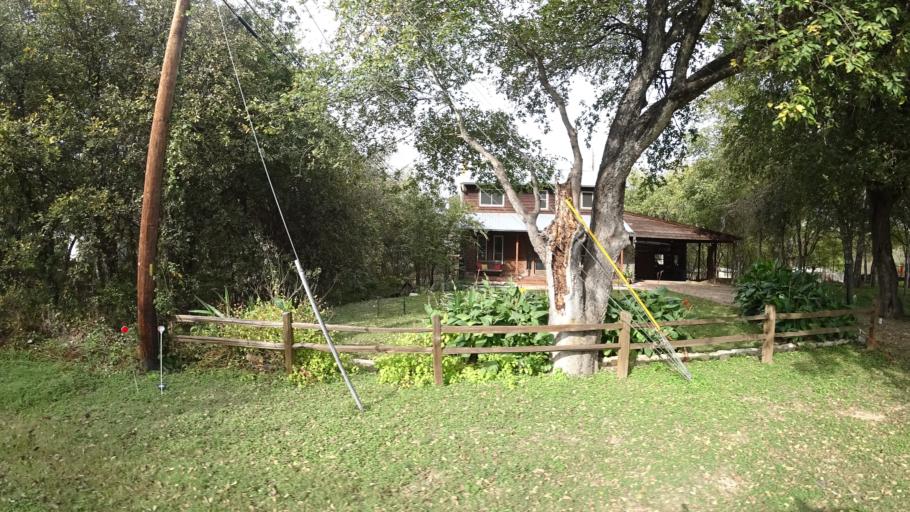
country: US
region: Texas
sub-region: Travis County
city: Hudson Bend
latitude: 30.3835
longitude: -97.9114
